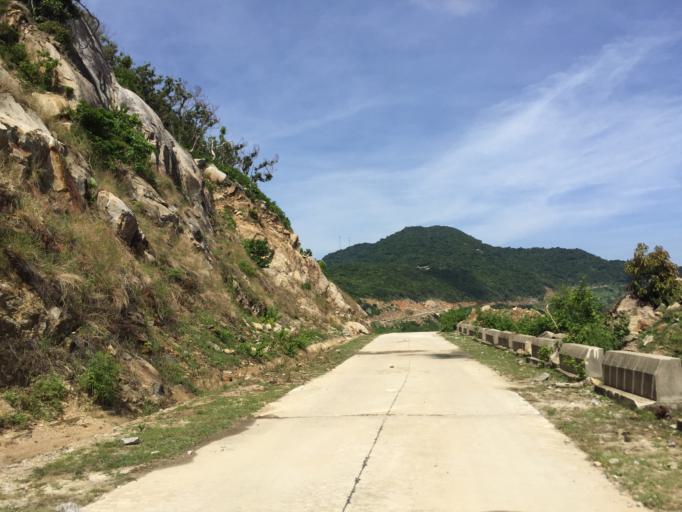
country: VN
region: Quang Nam
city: Hoi An
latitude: 15.9620
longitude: 108.5148
